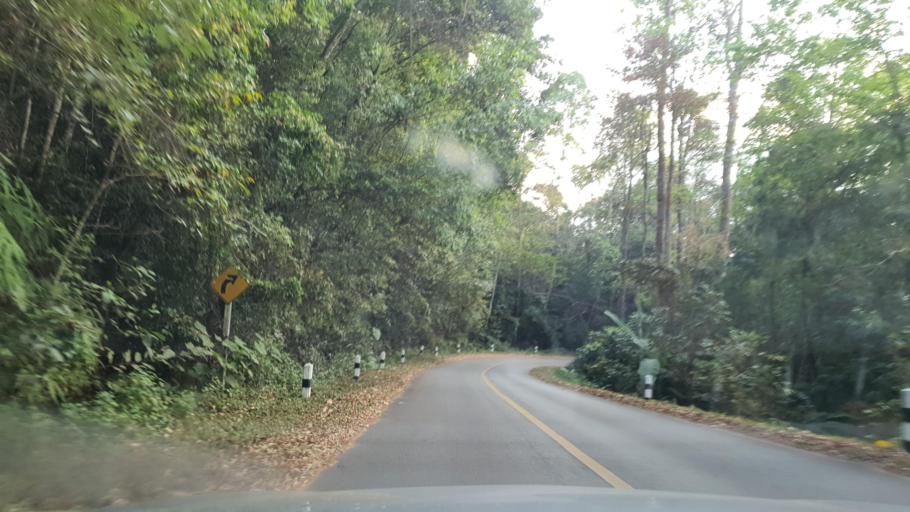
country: TH
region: Chiang Mai
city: Mae On
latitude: 18.9418
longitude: 99.3595
